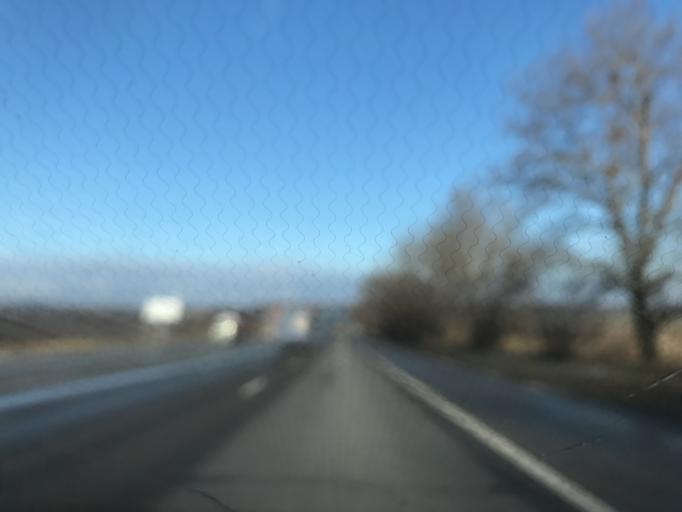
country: RU
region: Rostov
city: Grushevskaya
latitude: 47.5256
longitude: 39.9704
